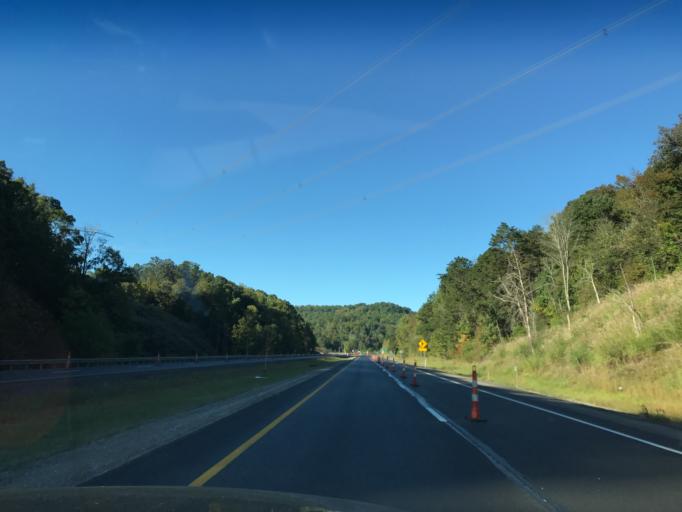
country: US
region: Ohio
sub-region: Washington County
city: Reno
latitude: 39.2476
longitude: -81.3583
